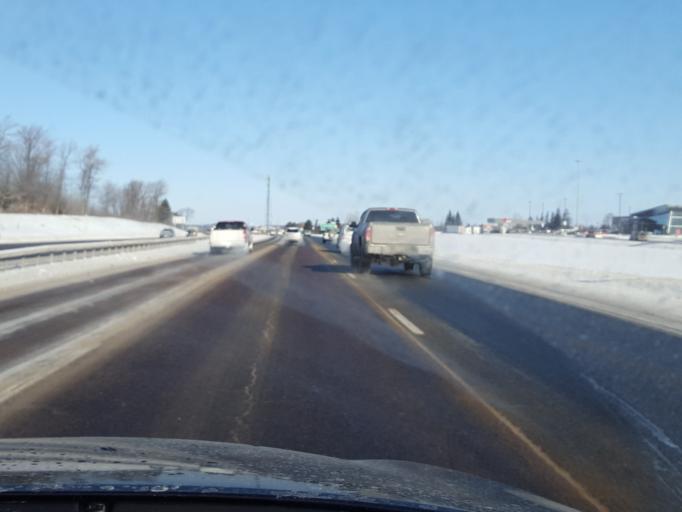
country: CA
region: Ontario
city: Barrie
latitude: 44.3493
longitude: -79.6881
